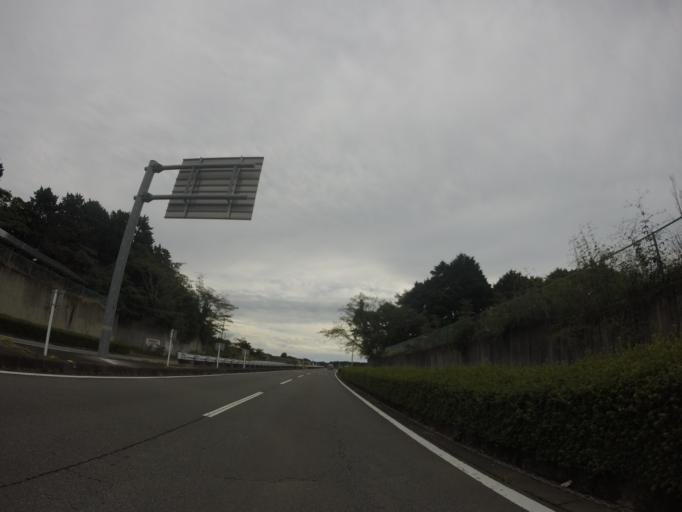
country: JP
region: Shizuoka
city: Fuji
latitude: 35.2004
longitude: 138.6763
